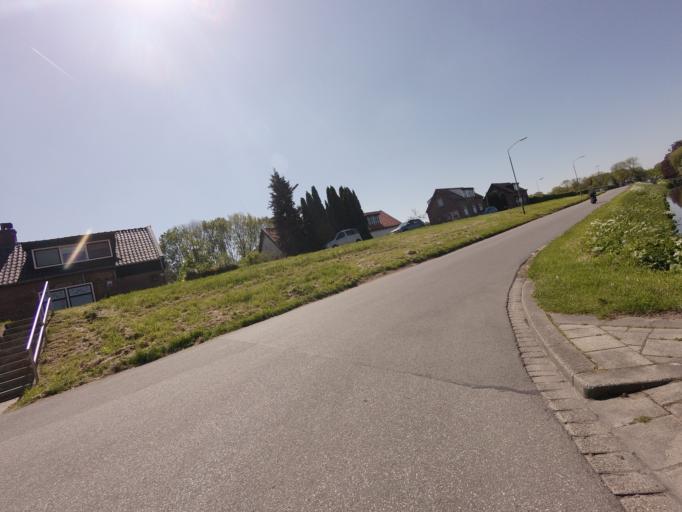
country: NL
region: South Holland
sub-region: Gemeente Dordrecht
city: Dordrecht
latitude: 51.7842
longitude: 4.6923
